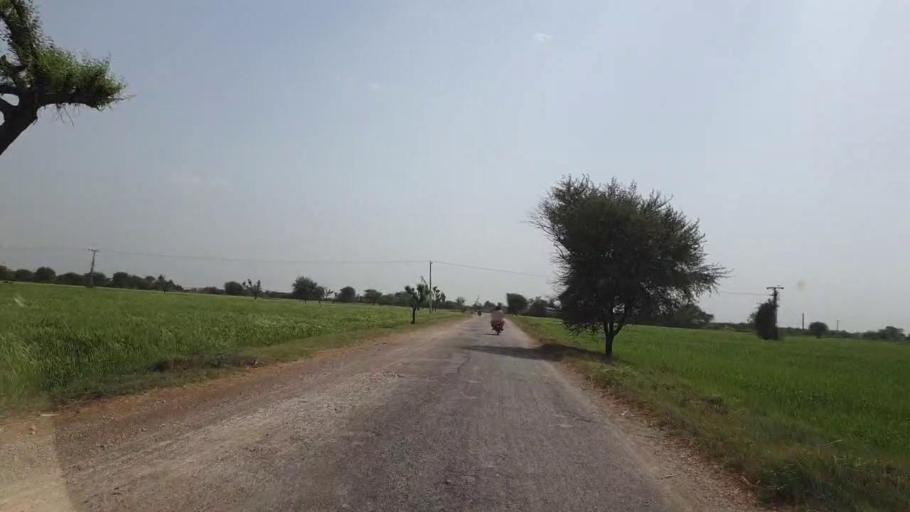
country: PK
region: Sindh
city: Tando Ghulam Ali
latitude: 25.0676
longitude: 68.8230
